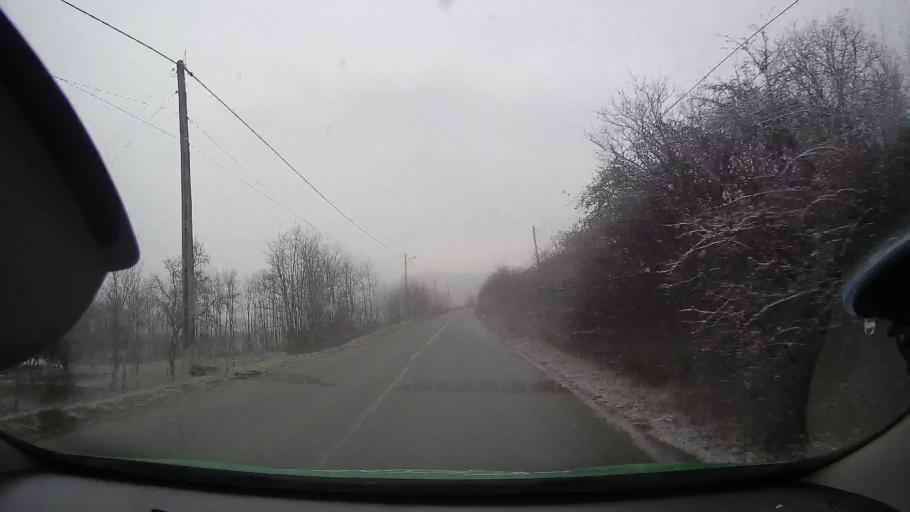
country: RO
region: Alba
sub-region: Comuna Noslac
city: Noslac
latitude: 46.3581
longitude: 23.9311
